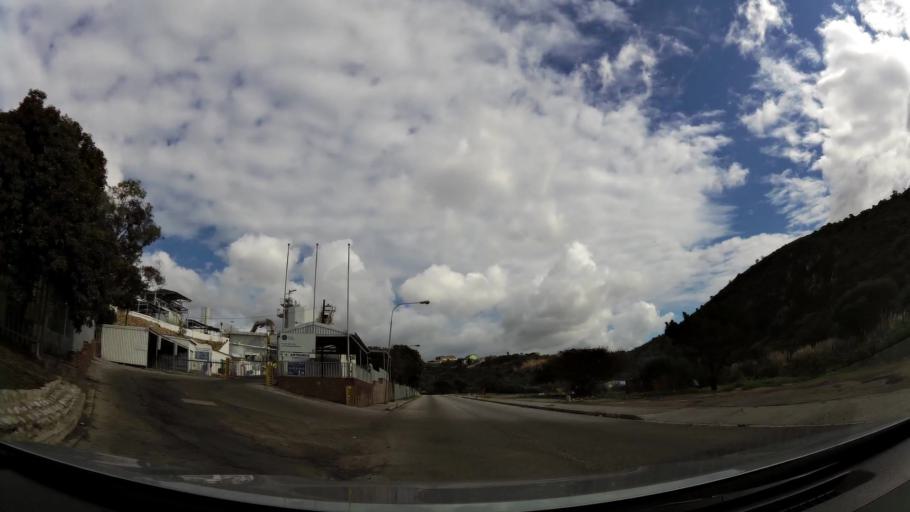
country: ZA
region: Eastern Cape
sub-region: Nelson Mandela Bay Metropolitan Municipality
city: Port Elizabeth
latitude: -33.9301
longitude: 25.5555
